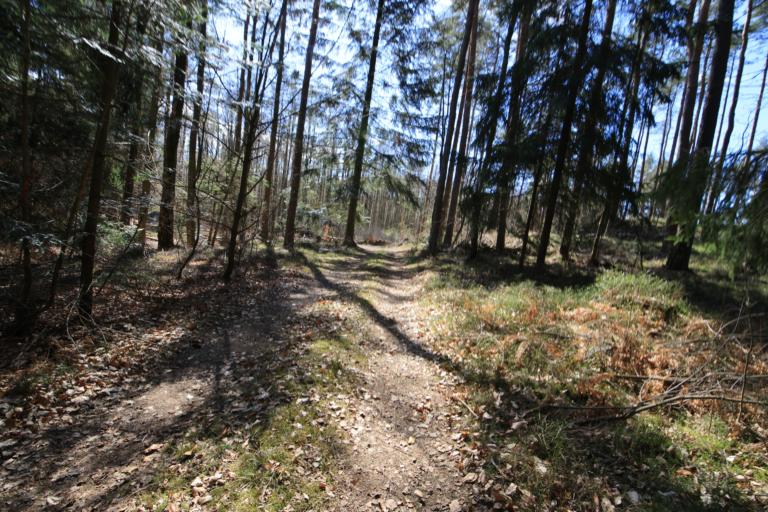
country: SE
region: Halland
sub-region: Varbergs Kommun
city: Varberg
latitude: 57.1910
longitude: 12.2356
